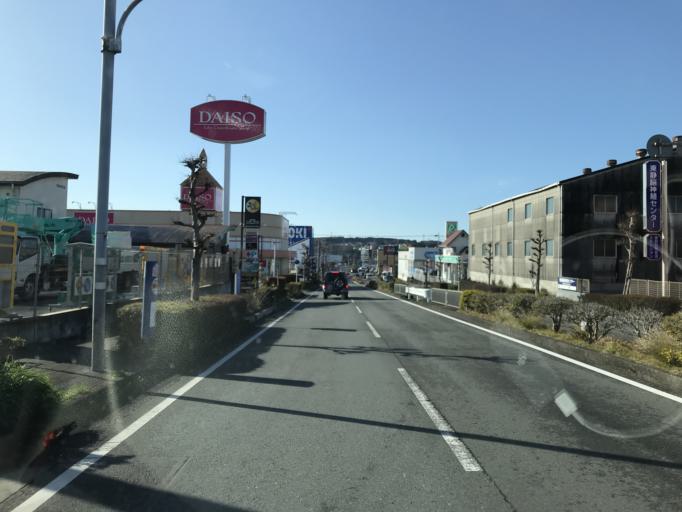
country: JP
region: Shizuoka
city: Fujinomiya
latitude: 35.2179
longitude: 138.6284
